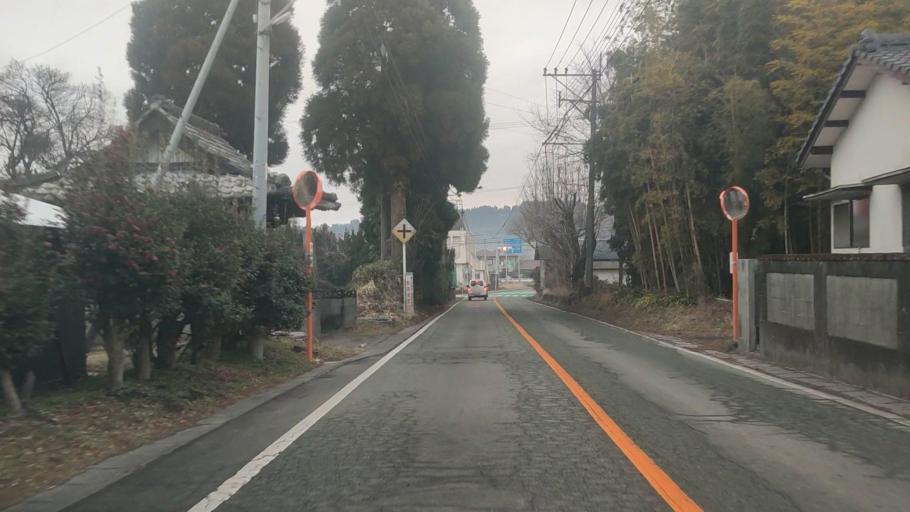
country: JP
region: Kumamoto
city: Aso
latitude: 32.9361
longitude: 131.1378
